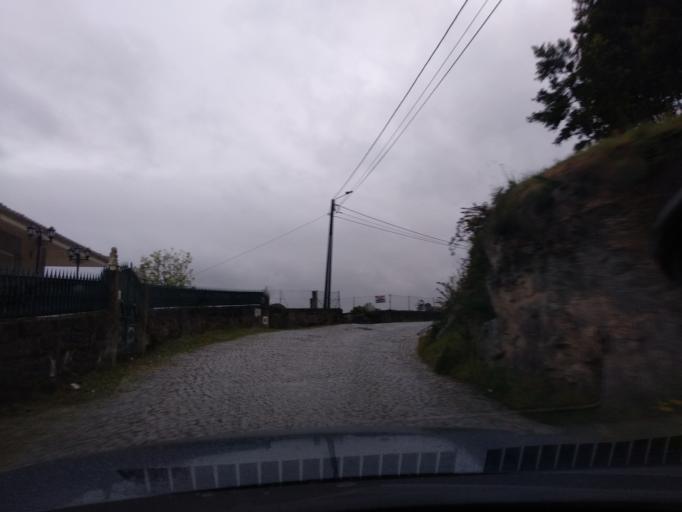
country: PT
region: Porto
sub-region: Penafiel
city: Penafiel
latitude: 41.1912
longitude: -8.2956
